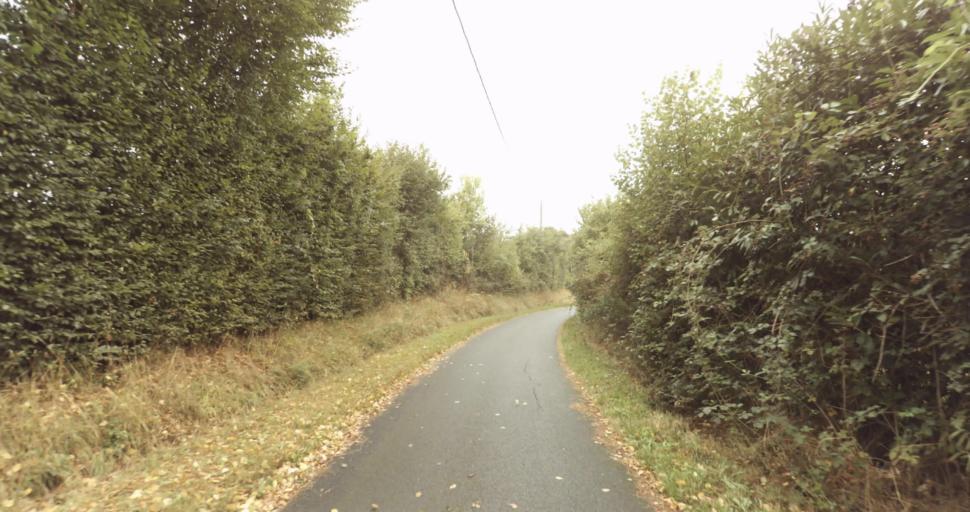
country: FR
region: Lower Normandy
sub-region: Departement de l'Orne
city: Sainte-Gauburge-Sainte-Colombe
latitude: 48.7072
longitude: 0.4498
